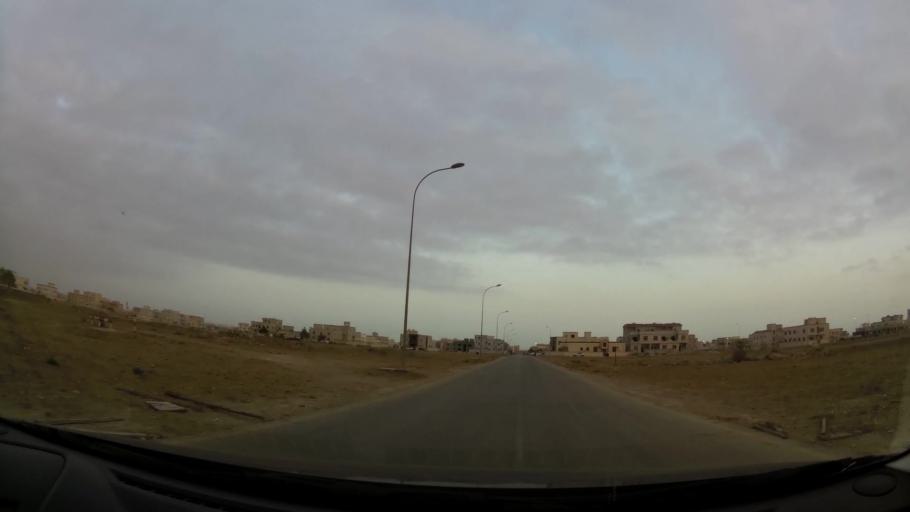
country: OM
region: Zufar
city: Salalah
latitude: 17.0356
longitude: 54.0212
